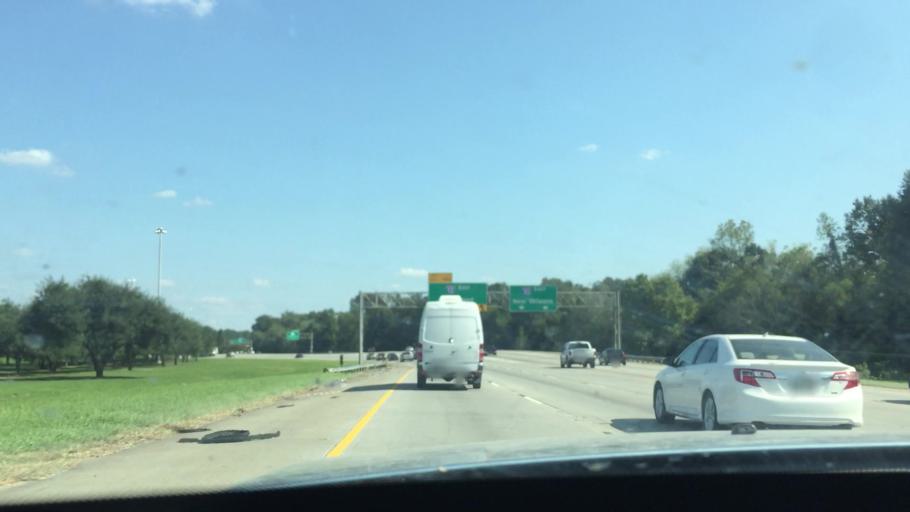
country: US
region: Louisiana
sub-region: East Baton Rouge Parish
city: Westminster
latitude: 30.4198
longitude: -91.1214
